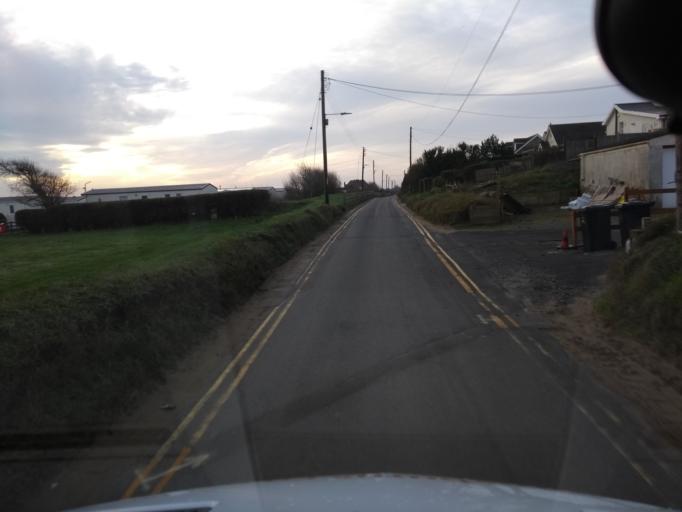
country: GB
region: England
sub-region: North Somerset
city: Weston-super-Mare
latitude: 51.3102
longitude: -3.0099
